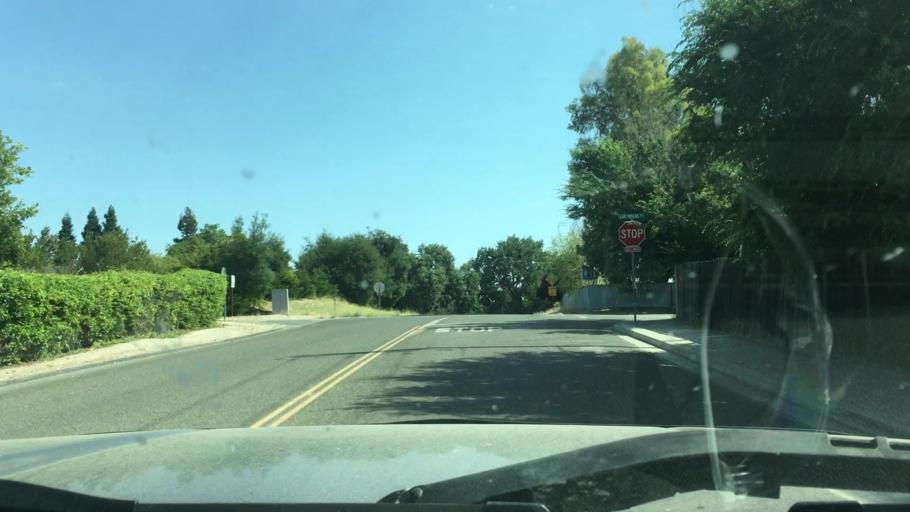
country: US
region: California
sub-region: San Luis Obispo County
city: Templeton
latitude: 35.5541
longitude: -120.7267
